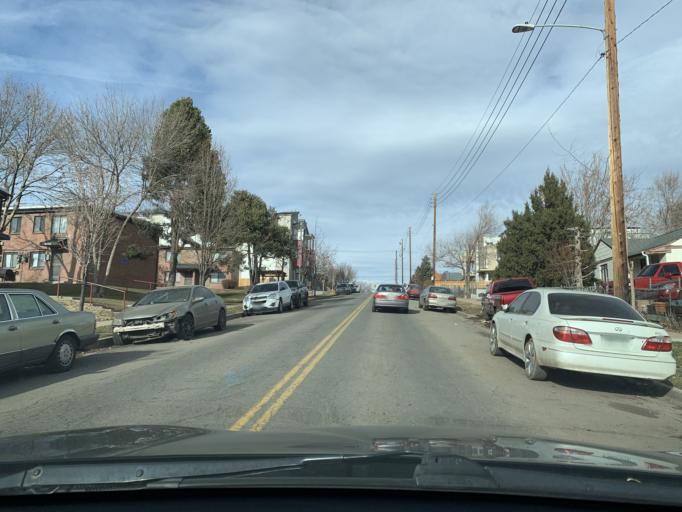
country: US
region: Colorado
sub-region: Jefferson County
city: Edgewater
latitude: 39.7370
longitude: -105.0322
